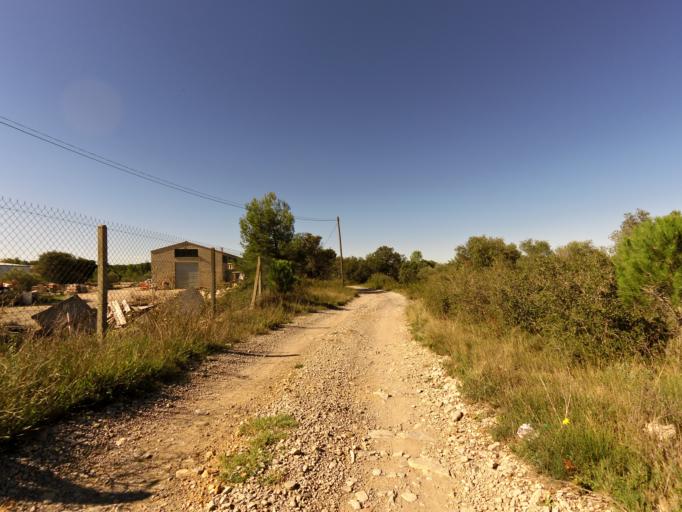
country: FR
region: Languedoc-Roussillon
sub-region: Departement du Gard
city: Aubais
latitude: 43.7433
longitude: 4.1416
